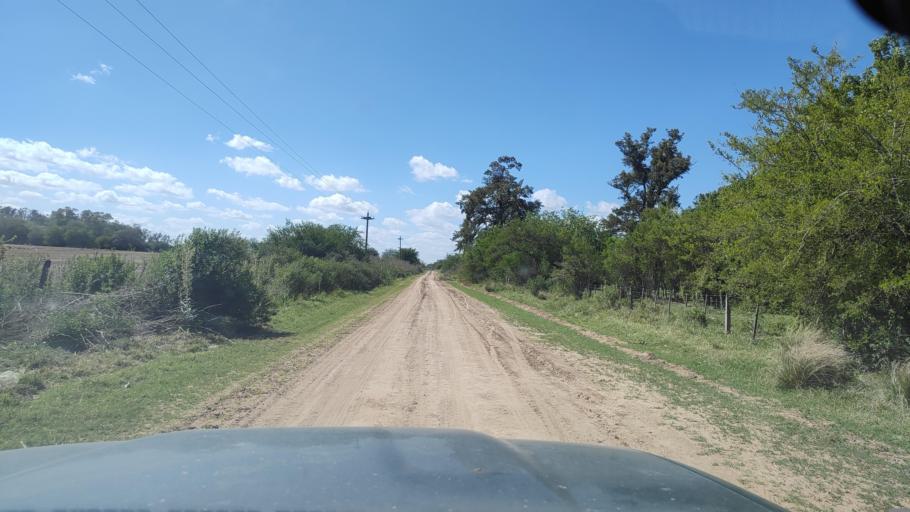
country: AR
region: Buenos Aires
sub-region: Partido de Lujan
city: Lujan
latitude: -34.5224
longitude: -59.1575
